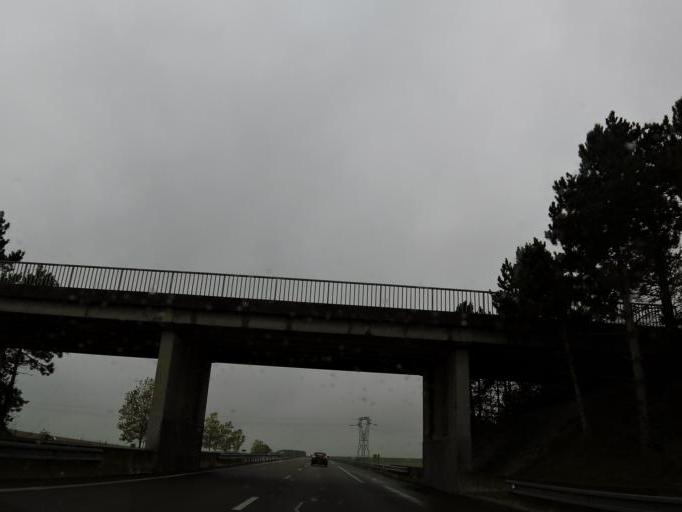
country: FR
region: Champagne-Ardenne
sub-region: Departement de la Marne
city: Saint-Memmie
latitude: 49.0344
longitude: 4.3864
